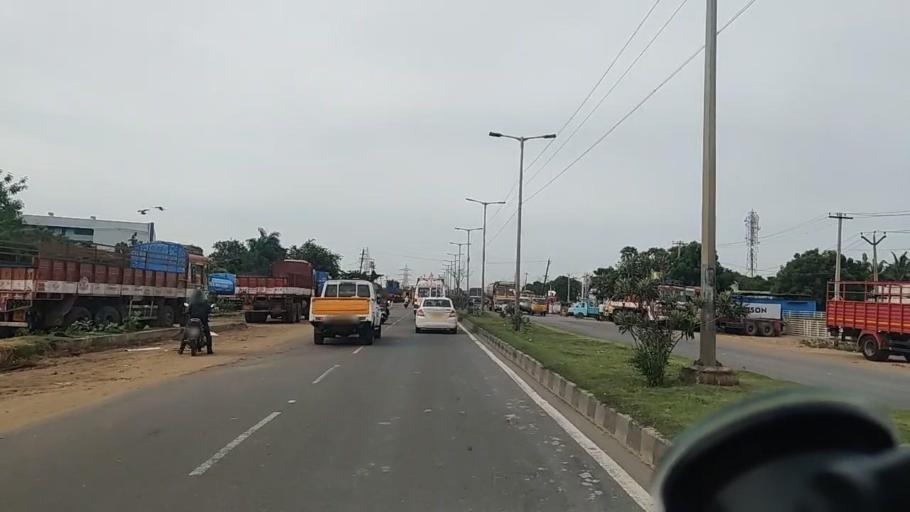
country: IN
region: Tamil Nadu
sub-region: Thiruvallur
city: Chinnasekkadu
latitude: 13.1651
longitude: 80.2286
